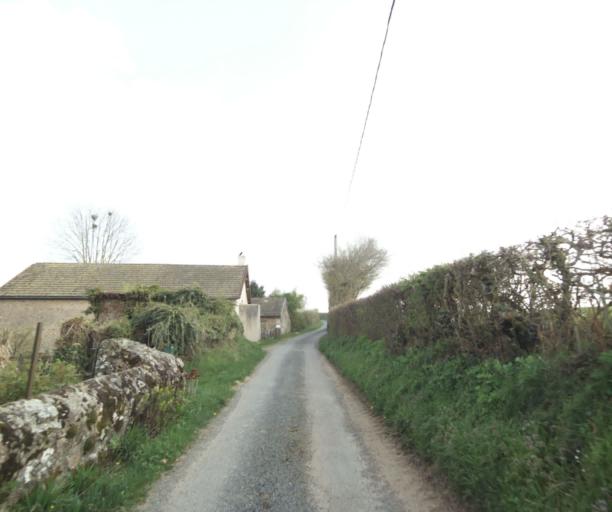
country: FR
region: Bourgogne
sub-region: Departement de Saone-et-Loire
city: Charolles
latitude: 46.4636
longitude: 4.4304
